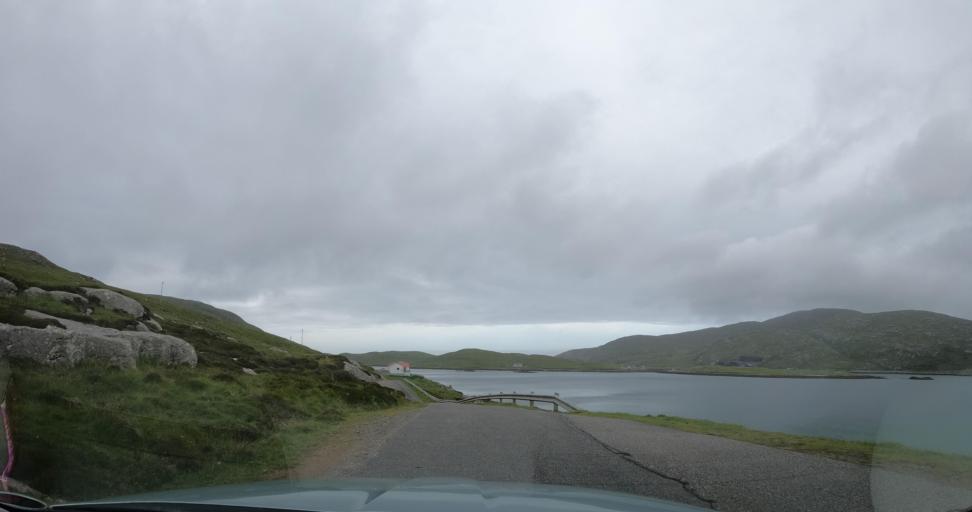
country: GB
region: Scotland
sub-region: Eilean Siar
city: Barra
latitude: 56.9366
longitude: -7.5209
